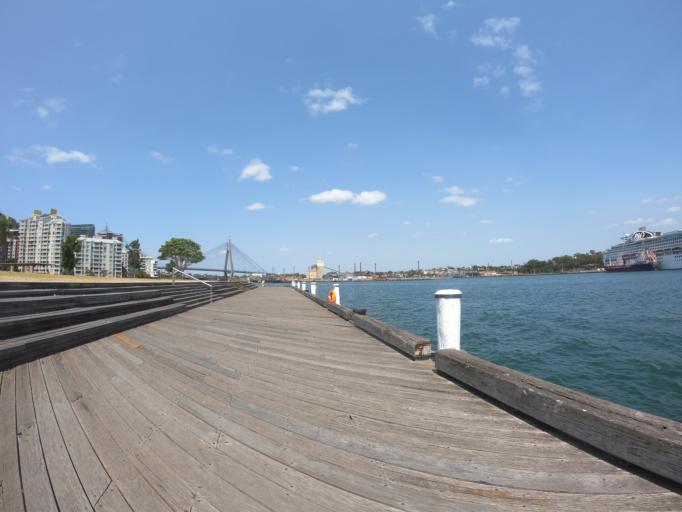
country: AU
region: New South Wales
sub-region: Leichhardt
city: Balmain East
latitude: -33.8636
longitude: 151.1914
